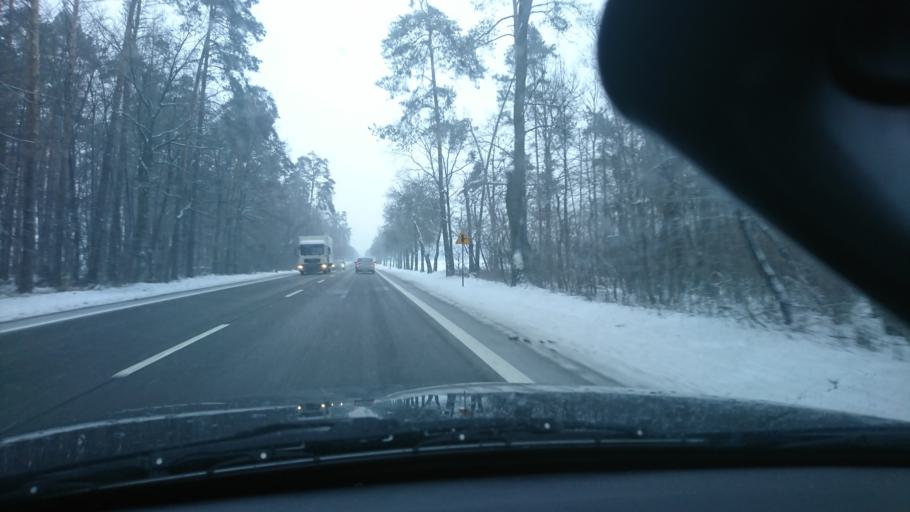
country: PL
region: Masovian Voivodeship
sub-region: Powiat ciechanowski
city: Glinojeck
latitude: 52.8444
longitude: 20.2749
